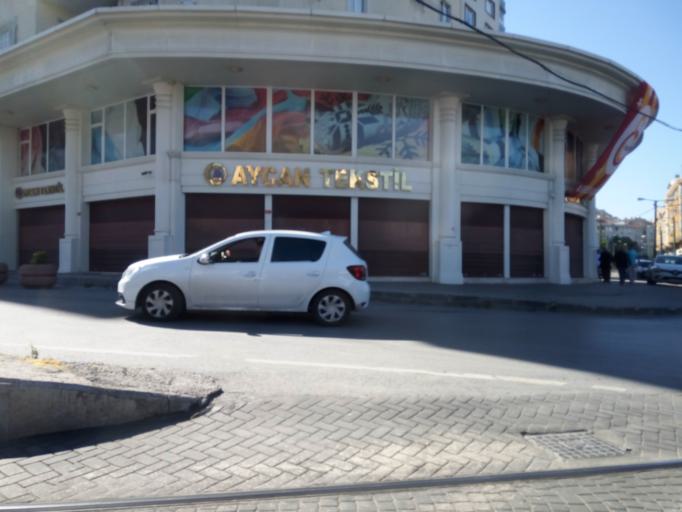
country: TR
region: Istanbul
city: Zeytinburnu
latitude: 41.0047
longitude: 28.9096
